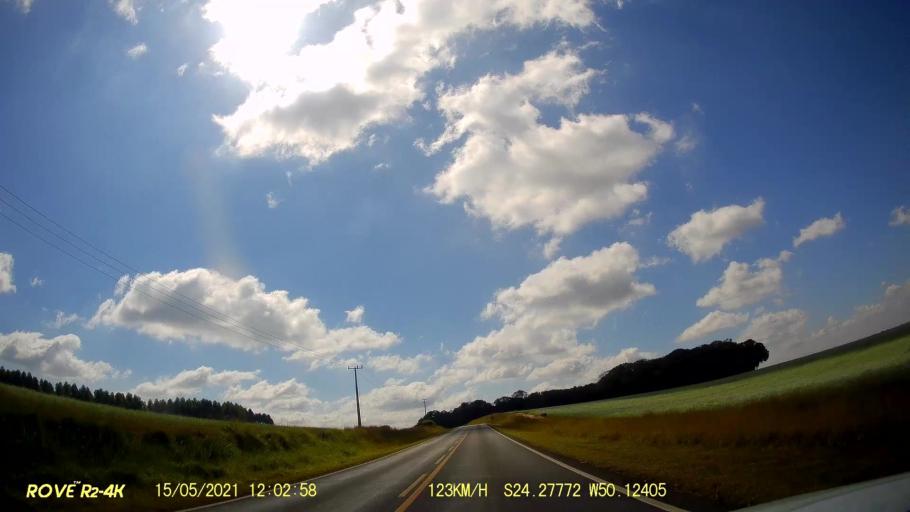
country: BR
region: Parana
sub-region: Pirai Do Sul
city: Pirai do Sul
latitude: -24.2777
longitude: -50.1240
